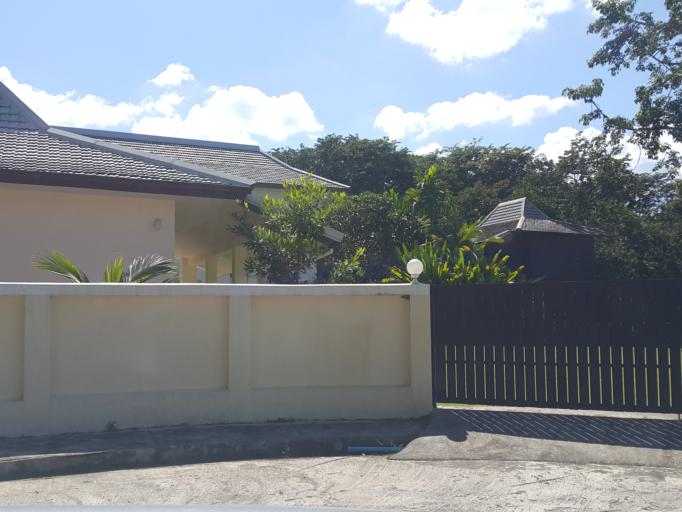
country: TH
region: Chiang Mai
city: San Sai
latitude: 18.8490
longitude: 99.0050
